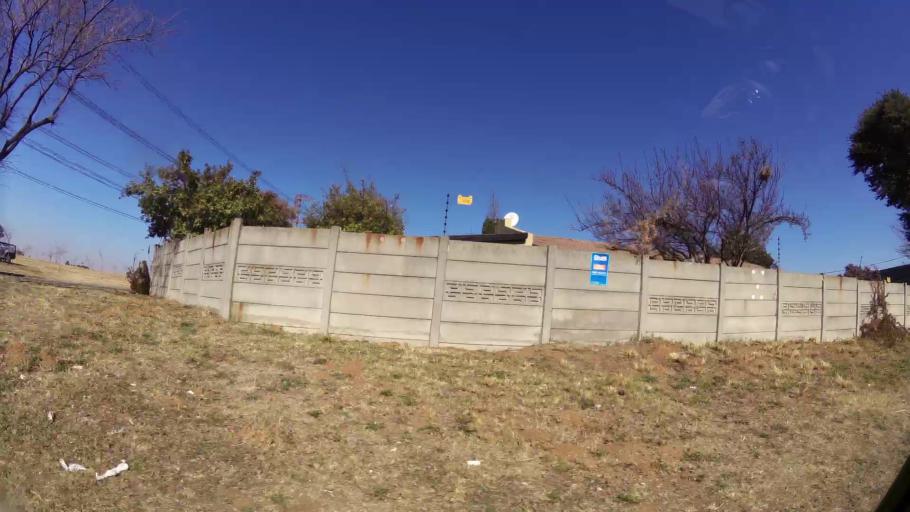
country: ZA
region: Gauteng
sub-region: Ekurhuleni Metropolitan Municipality
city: Germiston
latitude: -26.2417
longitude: 28.1050
